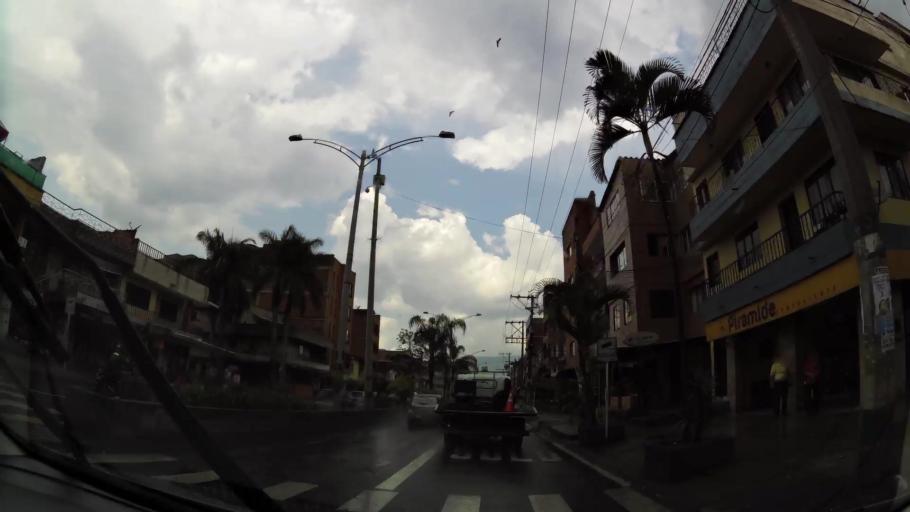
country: CO
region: Antioquia
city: Itagui
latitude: 6.1851
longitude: -75.5963
